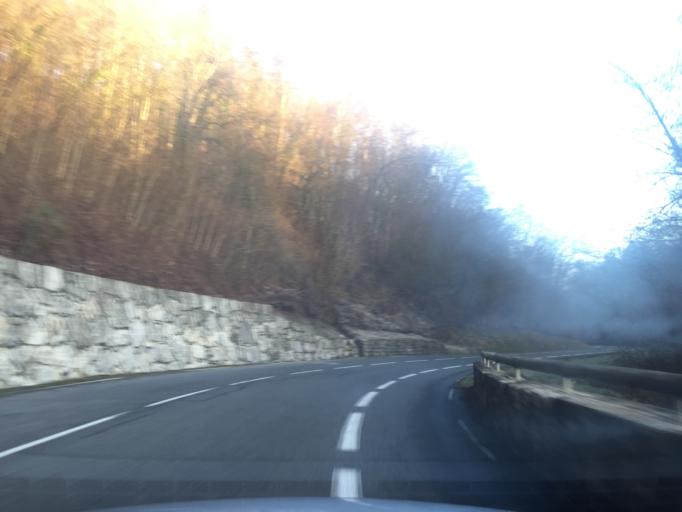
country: FR
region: Rhone-Alpes
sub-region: Departement de la Savoie
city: Gresy-sur-Aix
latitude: 45.7375
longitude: 5.9679
